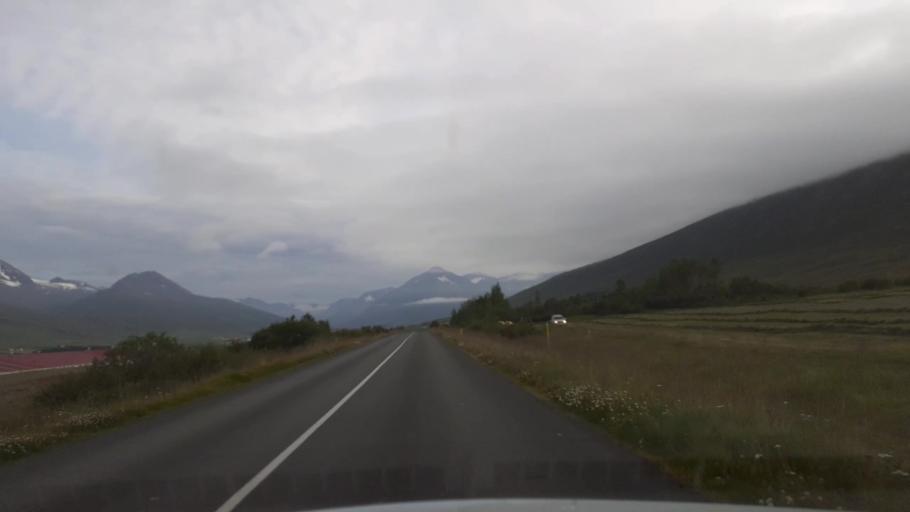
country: IS
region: Northeast
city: Dalvik
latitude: 65.9524
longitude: -18.5527
